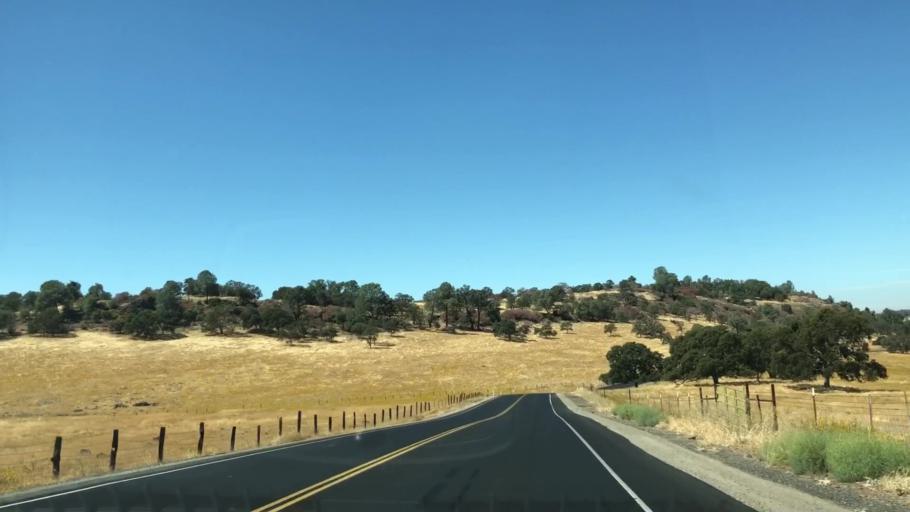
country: US
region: California
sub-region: Tuolumne County
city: Jamestown
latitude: 37.8812
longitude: -120.4753
